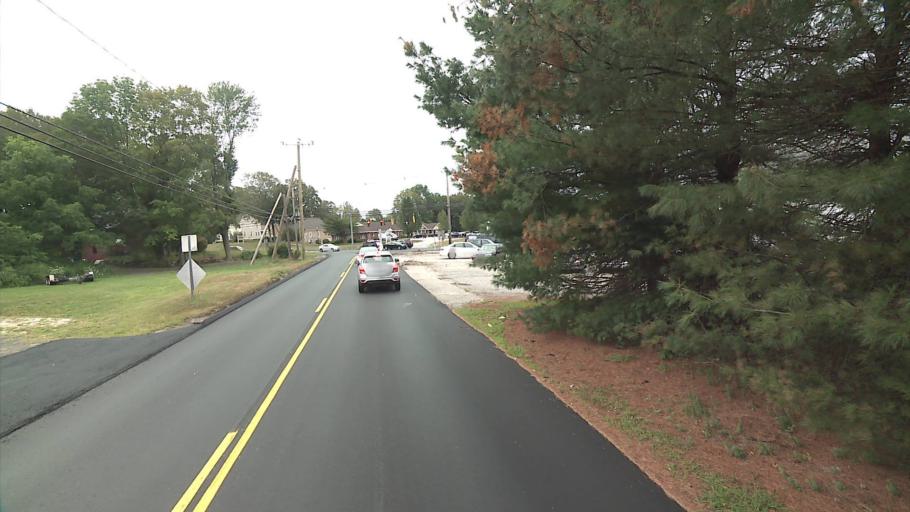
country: US
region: Connecticut
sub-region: New London County
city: Colchester
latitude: 41.5791
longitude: -72.3365
